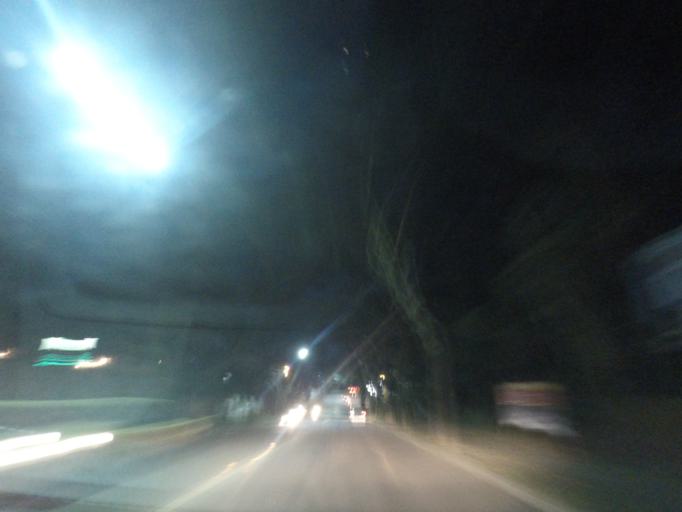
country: BR
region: Parana
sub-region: Curitiba
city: Curitiba
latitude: -25.4065
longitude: -49.3236
